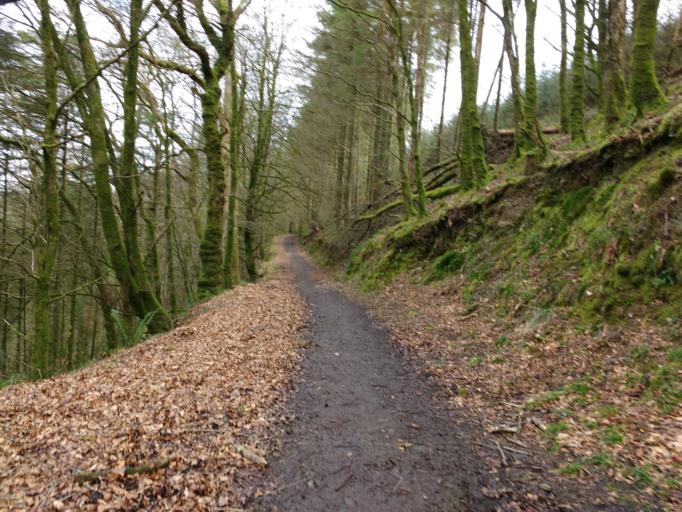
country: IE
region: Leinster
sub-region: Kilkenny
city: Callan
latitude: 52.6605
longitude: -7.5360
